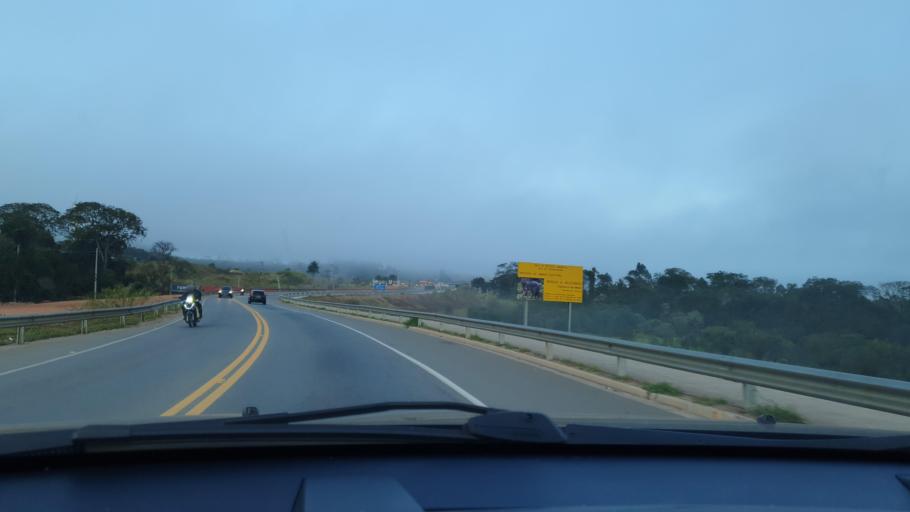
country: BR
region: Sao Paulo
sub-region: Vargem Grande Paulista
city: Vargem Grande Paulista
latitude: -23.6411
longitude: -47.0573
